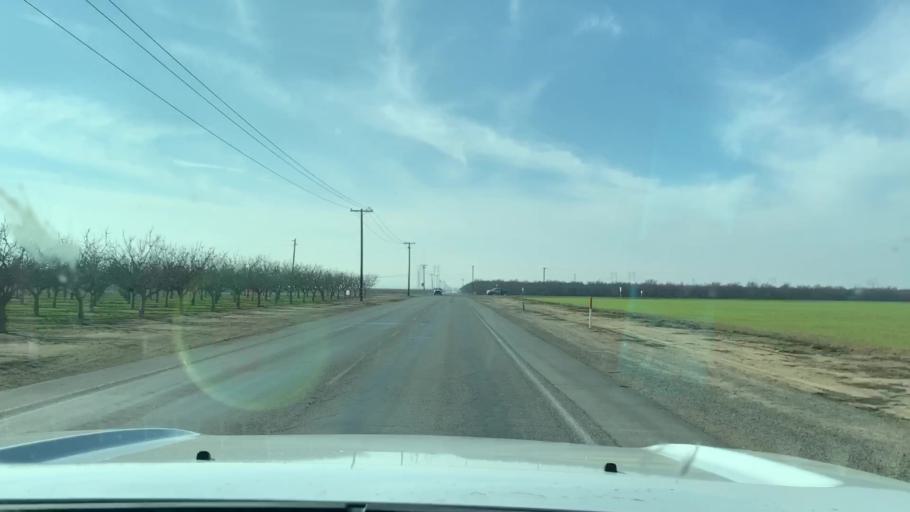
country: US
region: California
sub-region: Kern County
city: Buttonwillow
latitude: 35.4424
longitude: -119.4719
